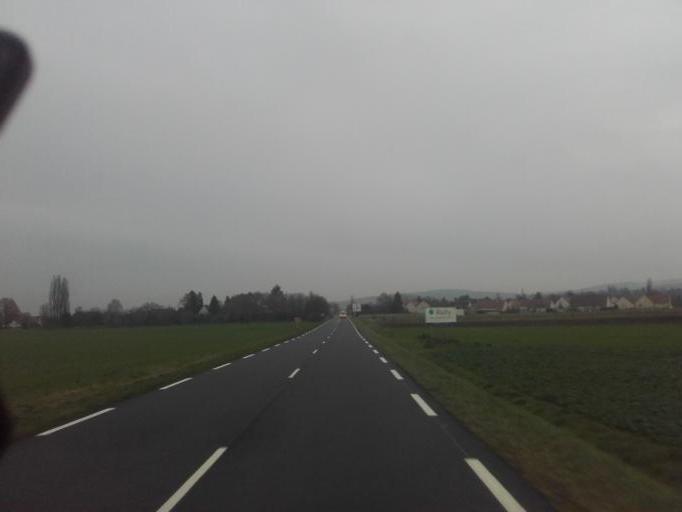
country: FR
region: Bourgogne
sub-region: Departement de Saone-et-Loire
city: Rully
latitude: 46.8836
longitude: 4.7523
